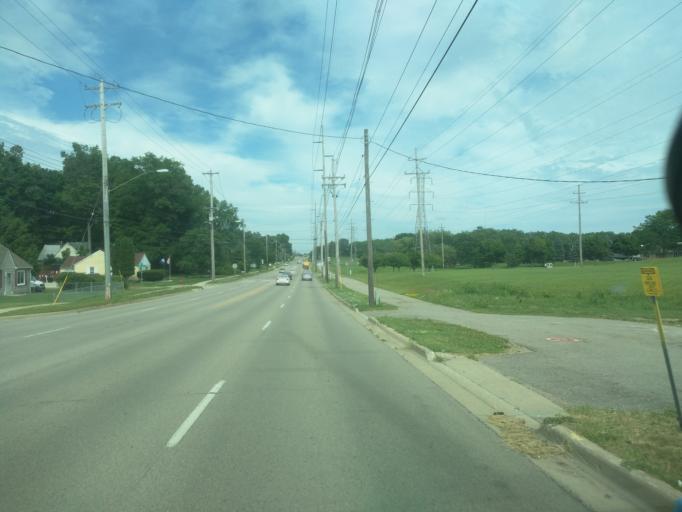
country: US
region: Michigan
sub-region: Ingham County
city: Holt
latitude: 42.6829
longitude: -84.5289
